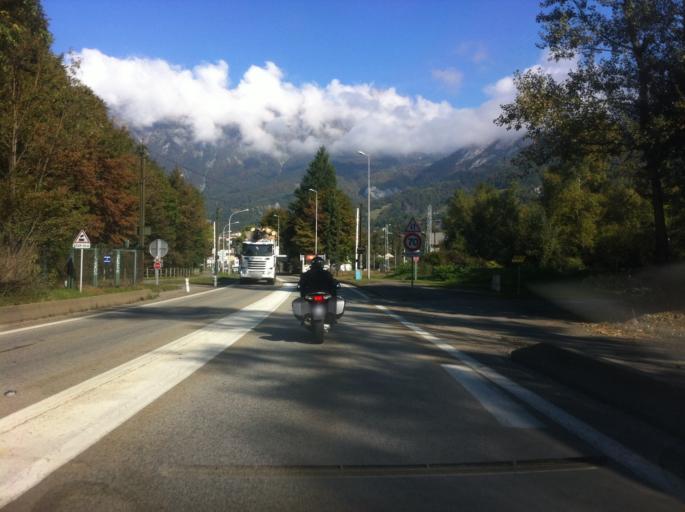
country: FR
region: Rhone-Alpes
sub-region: Departement de la Savoie
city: Ugine
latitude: 45.7390
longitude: 6.4236
